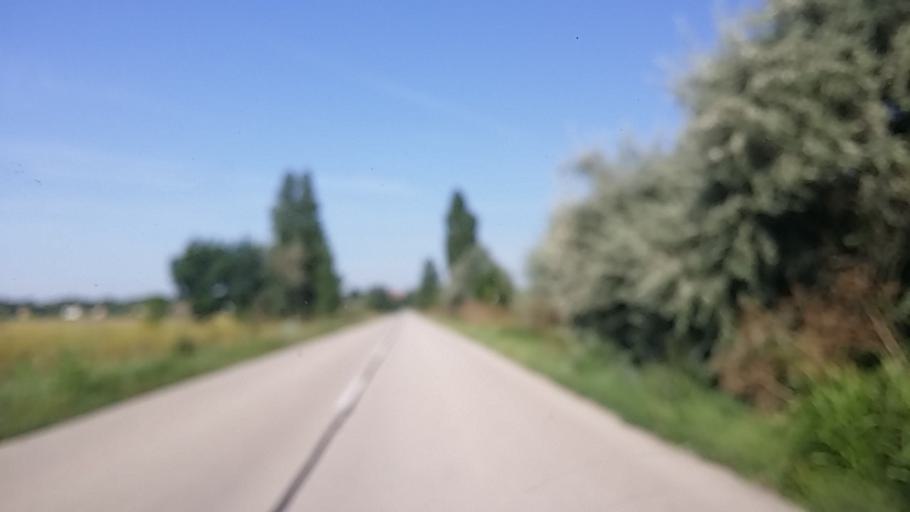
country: HU
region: Fejer
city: Adony
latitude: 47.1405
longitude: 18.8488
